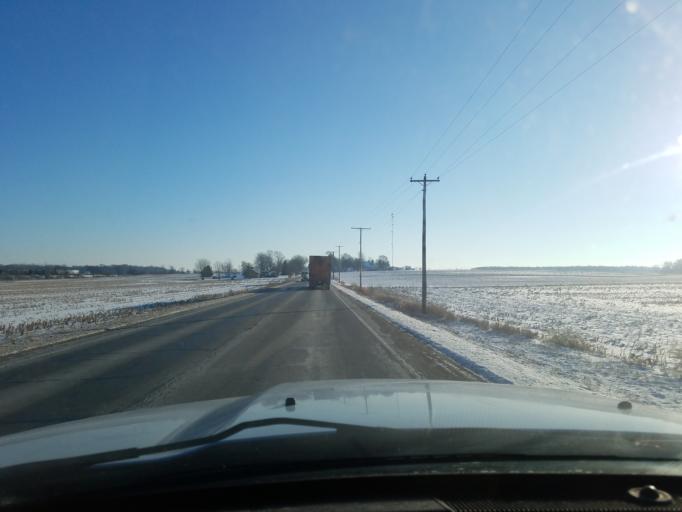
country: US
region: Indiana
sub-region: Noble County
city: Albion
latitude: 41.4531
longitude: -85.4369
